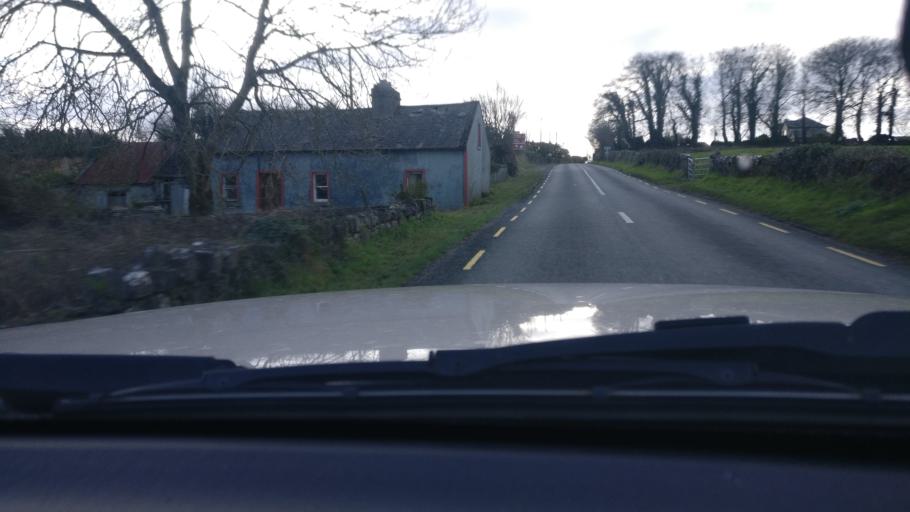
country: IE
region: Connaught
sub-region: County Galway
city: Ballinasloe
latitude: 53.3059
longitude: -8.2439
